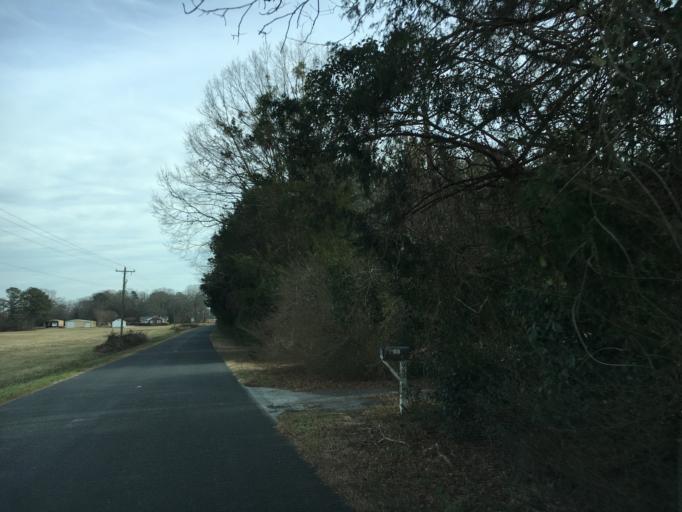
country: US
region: South Carolina
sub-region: Laurens County
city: Laurens
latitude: 34.3644
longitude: -81.9775
